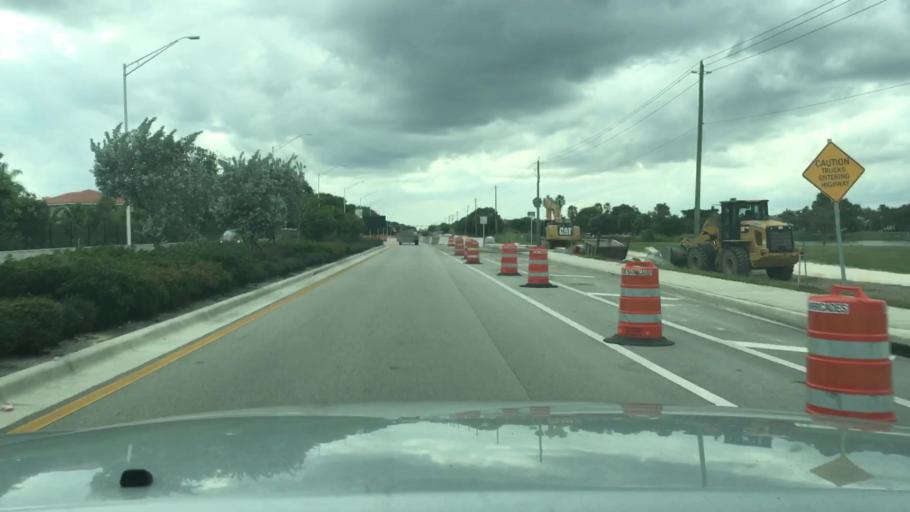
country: US
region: Florida
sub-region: Miami-Dade County
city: Country Club
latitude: 25.9932
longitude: -80.3465
